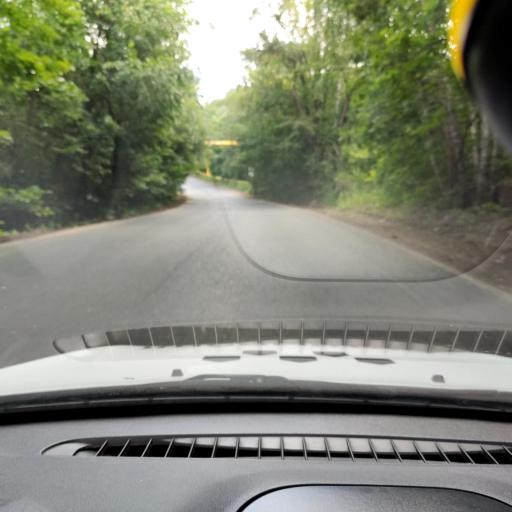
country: RU
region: Samara
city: Zhigulevsk
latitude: 53.3975
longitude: 49.4116
